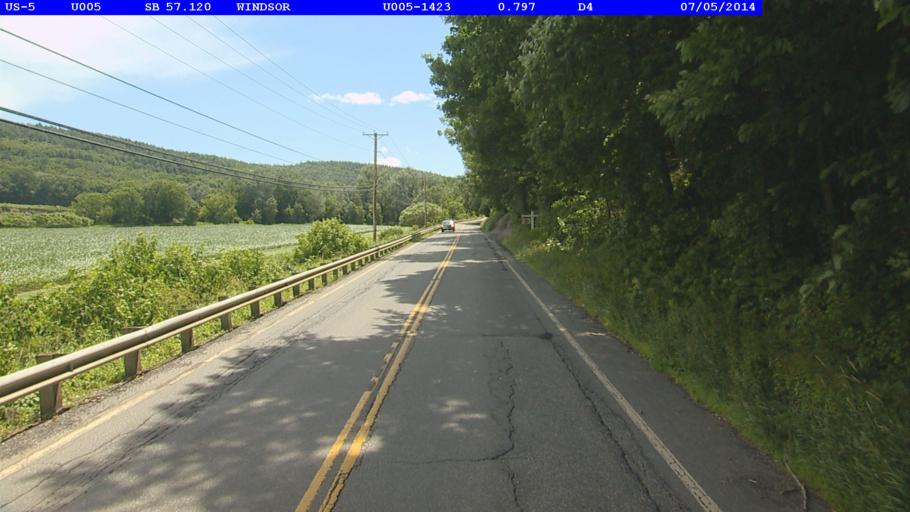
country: US
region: Vermont
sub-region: Windsor County
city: Windsor
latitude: 43.4401
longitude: -72.3980
